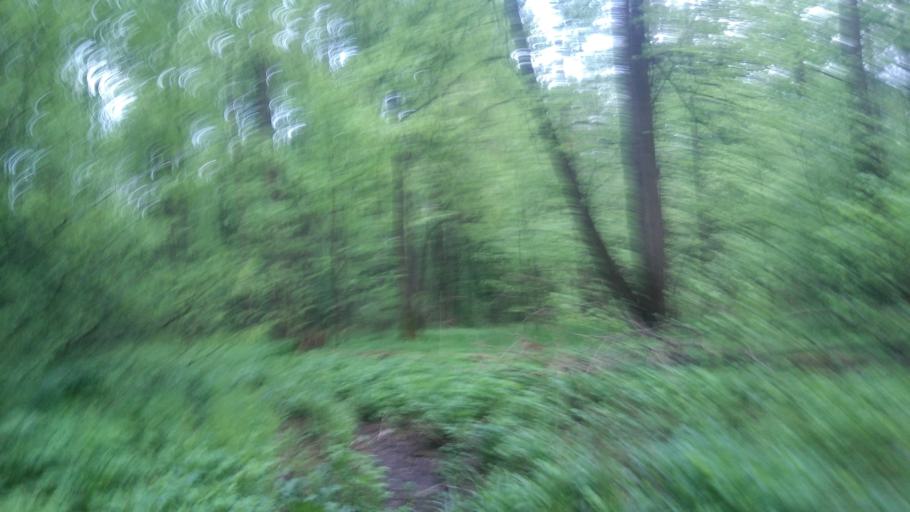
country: RU
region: Perm
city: Froly
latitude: 57.9671
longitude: 56.2926
